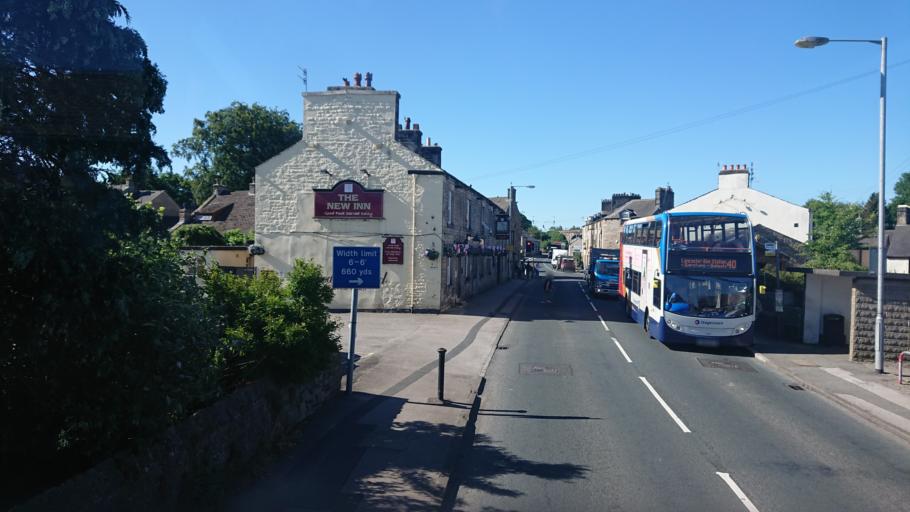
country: GB
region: England
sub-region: Lancashire
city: Galgate
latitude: 53.9924
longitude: -2.7889
